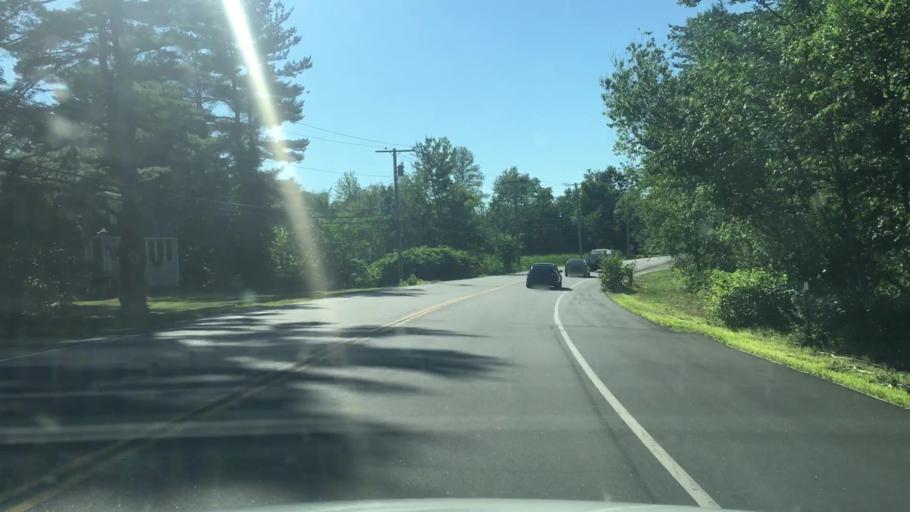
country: US
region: New Hampshire
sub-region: Rockingham County
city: Exeter
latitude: 43.0085
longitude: -70.9974
